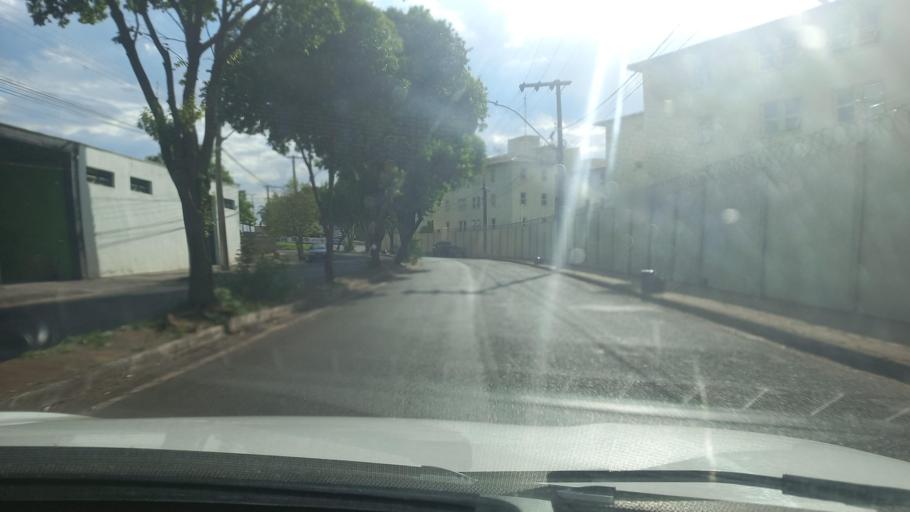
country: BR
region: Minas Gerais
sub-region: Uberaba
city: Uberaba
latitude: -19.7591
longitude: -47.9095
